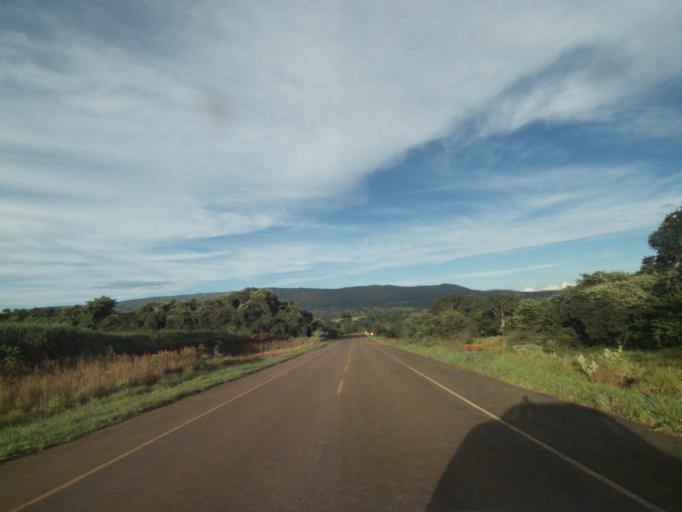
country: BR
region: Goias
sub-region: Jaragua
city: Jaragua
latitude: -15.8459
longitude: -49.3672
